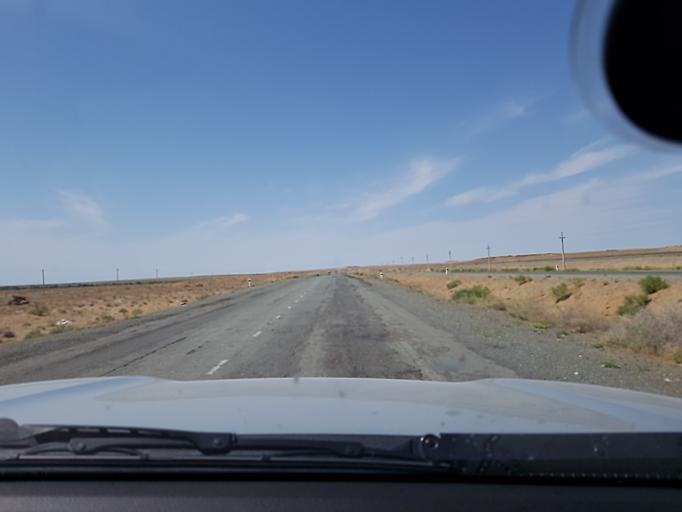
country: UZ
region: Karakalpakstan
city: Mang'it Shahri
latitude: 42.3186
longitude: 60.0336
